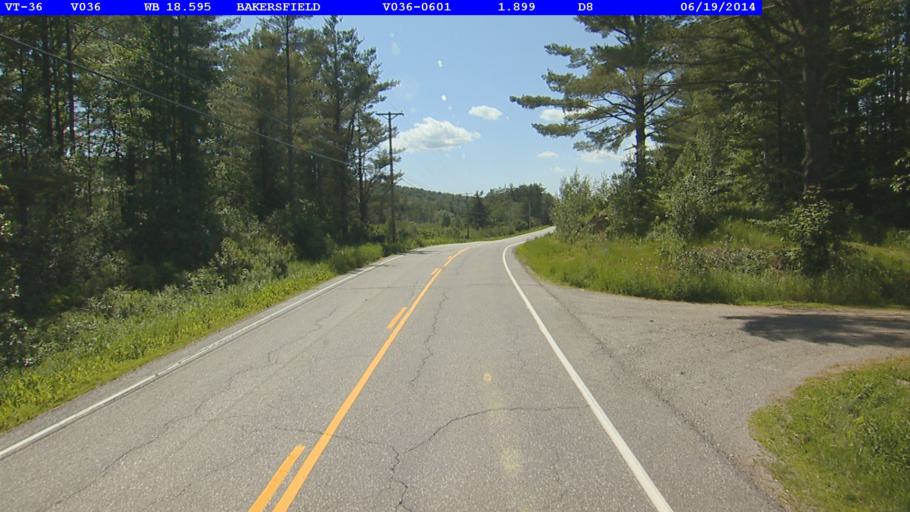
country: US
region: Vermont
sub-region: Franklin County
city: Enosburg Falls
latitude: 44.7806
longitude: -72.8131
